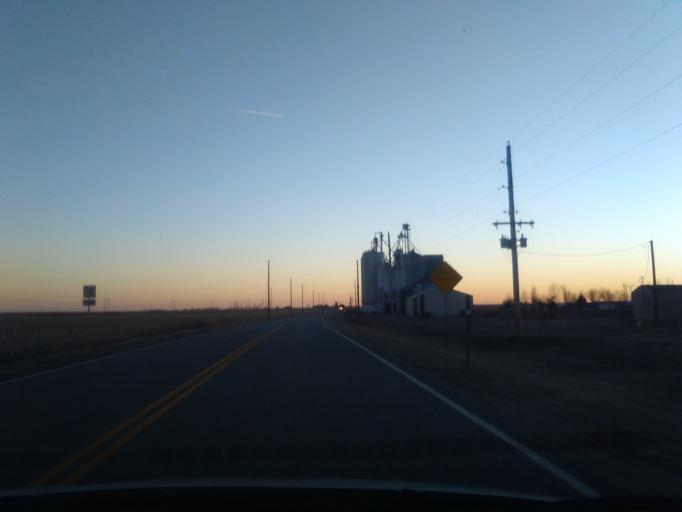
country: US
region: Nebraska
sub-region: Cheyenne County
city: Sidney
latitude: 40.9615
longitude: -103.1105
